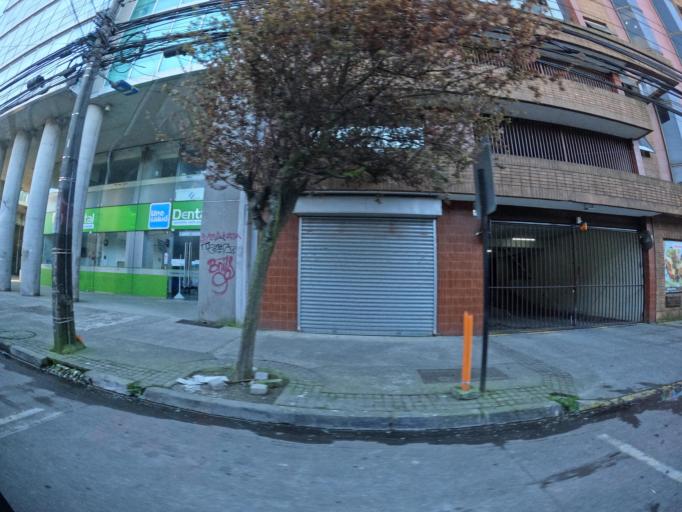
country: CL
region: Biobio
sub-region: Provincia de Concepcion
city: Concepcion
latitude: -36.8295
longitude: -73.0482
